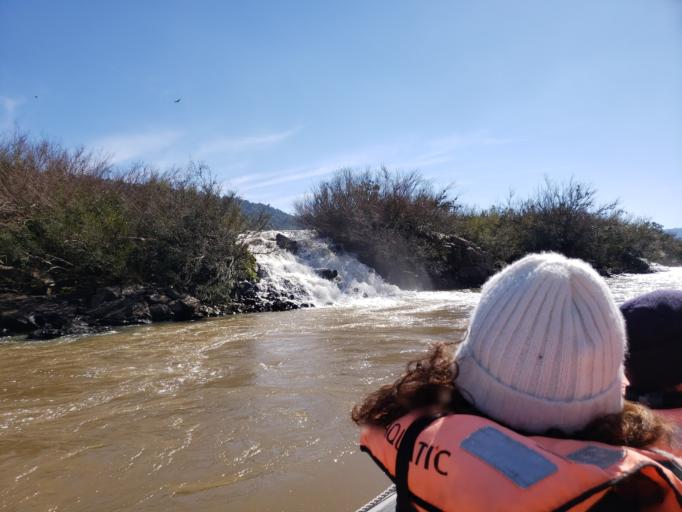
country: BR
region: Rio Grande do Sul
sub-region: Tres Passos
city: Tres Passos
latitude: -27.1533
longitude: -53.8888
